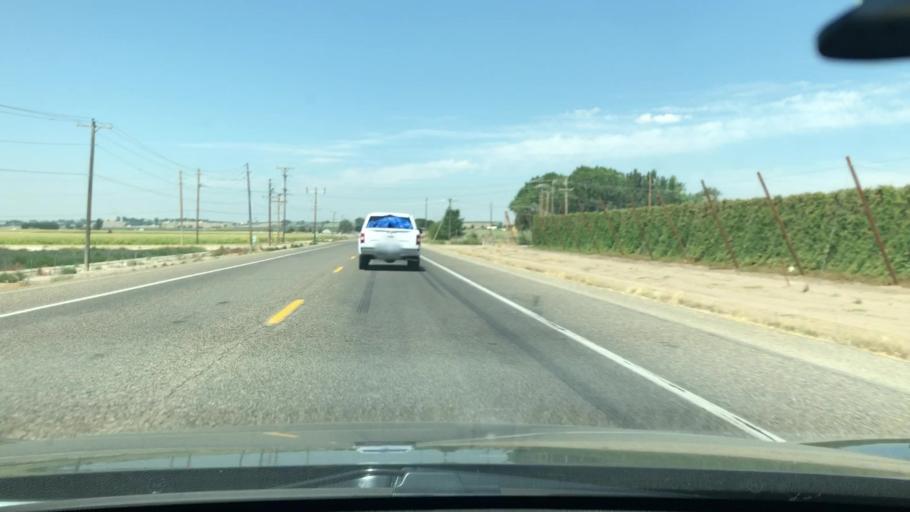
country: US
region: Idaho
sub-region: Owyhee County
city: Homedale
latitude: 43.6311
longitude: -116.9119
